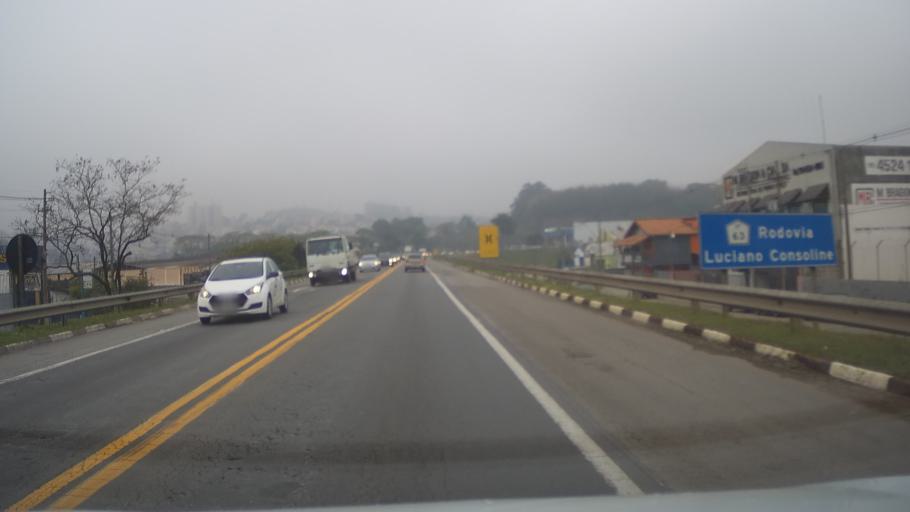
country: BR
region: Sao Paulo
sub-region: Itatiba
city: Itatiba
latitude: -23.0166
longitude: -46.8402
